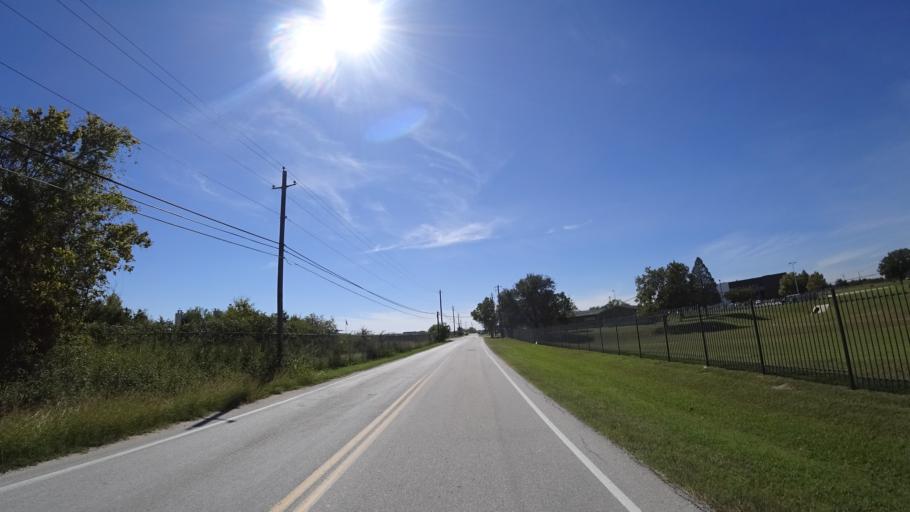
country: US
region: Texas
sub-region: Travis County
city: Austin
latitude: 30.1875
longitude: -97.7035
